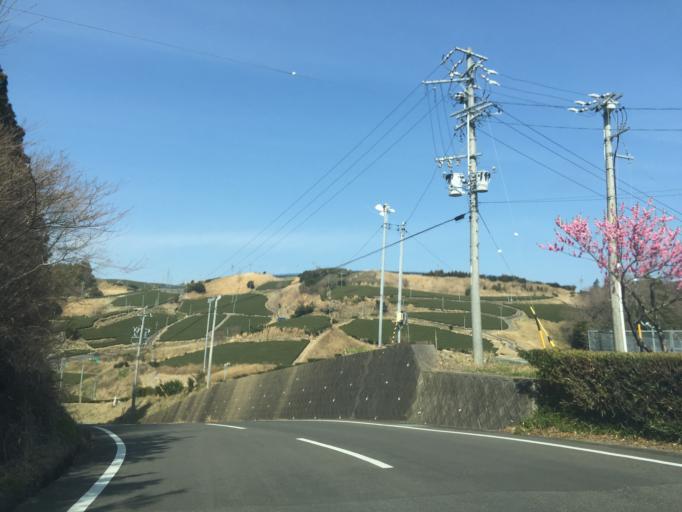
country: JP
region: Shizuoka
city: Kanaya
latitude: 34.8311
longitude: 138.0833
